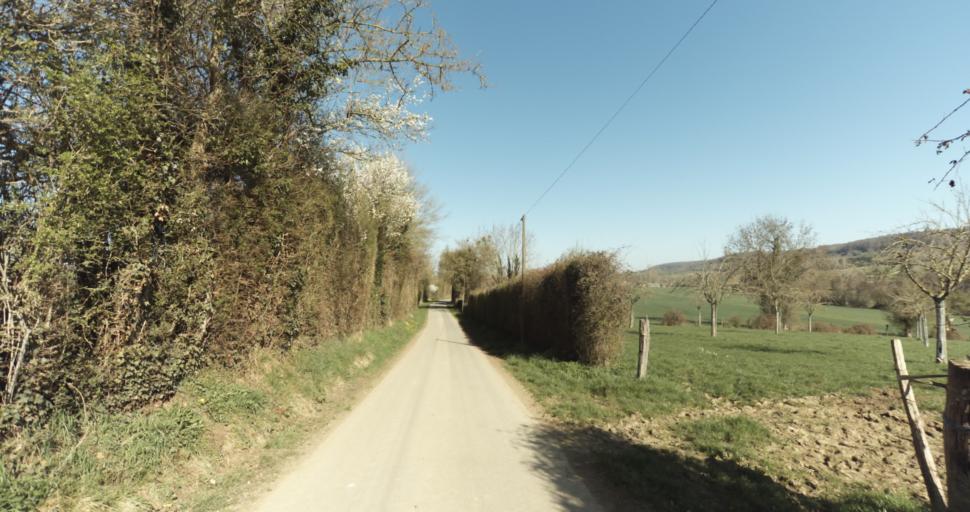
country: FR
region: Lower Normandy
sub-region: Departement du Calvados
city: Saint-Pierre-sur-Dives
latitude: 48.9693
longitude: 0.0381
